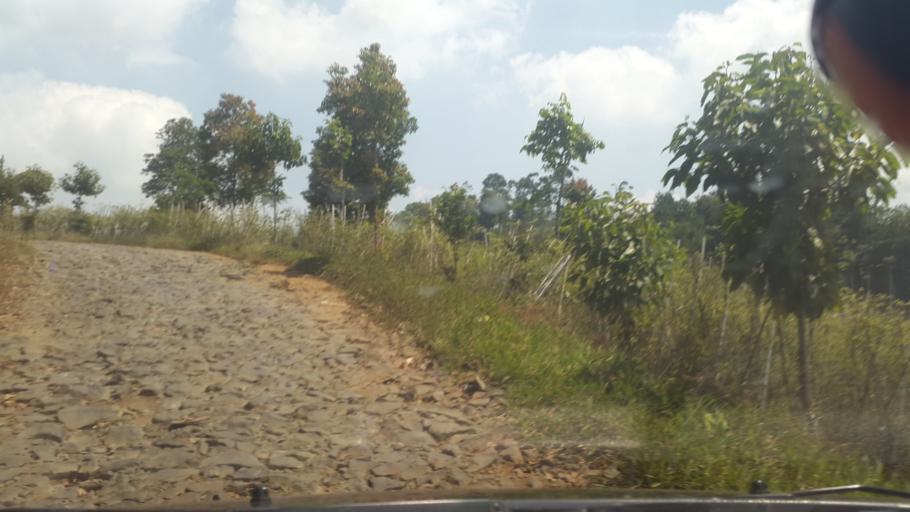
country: ID
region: West Java
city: Pasirhuni
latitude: -7.0253
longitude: 106.9928
